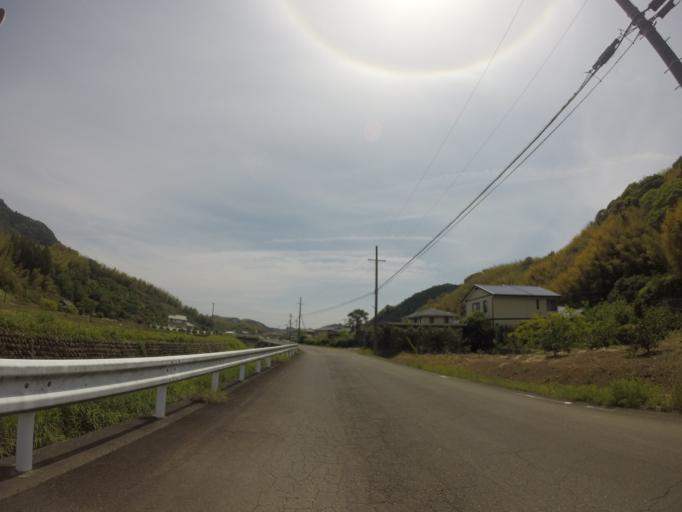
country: JP
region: Shizuoka
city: Fujieda
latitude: 34.9293
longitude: 138.2324
